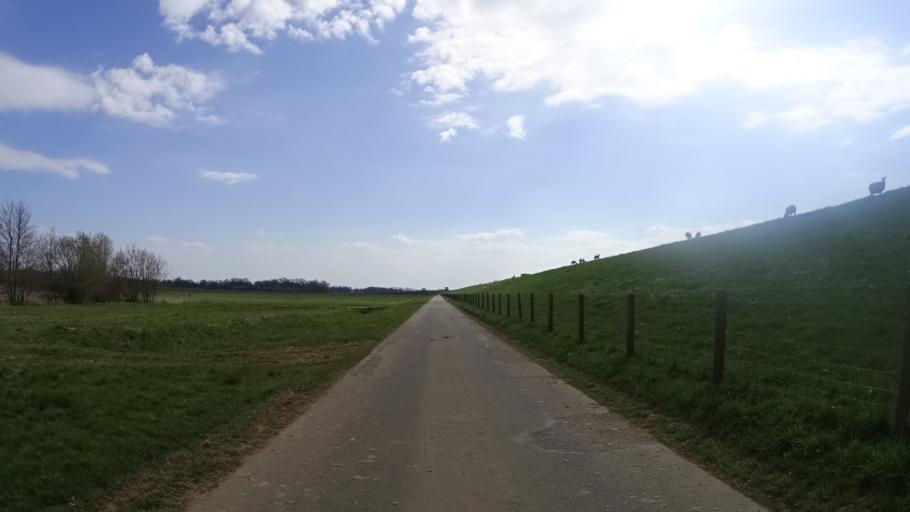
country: DE
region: Lower Saxony
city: Rhede
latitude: 53.0902
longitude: 7.2970
